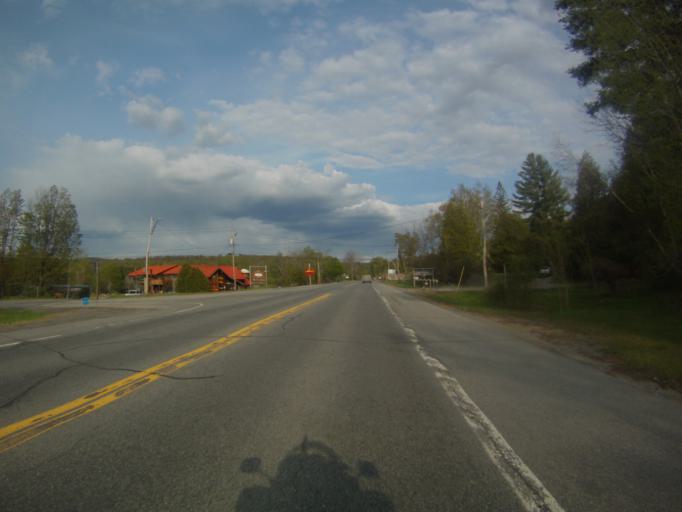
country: US
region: New York
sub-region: Warren County
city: Warrensburg
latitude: 43.6840
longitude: -73.9796
